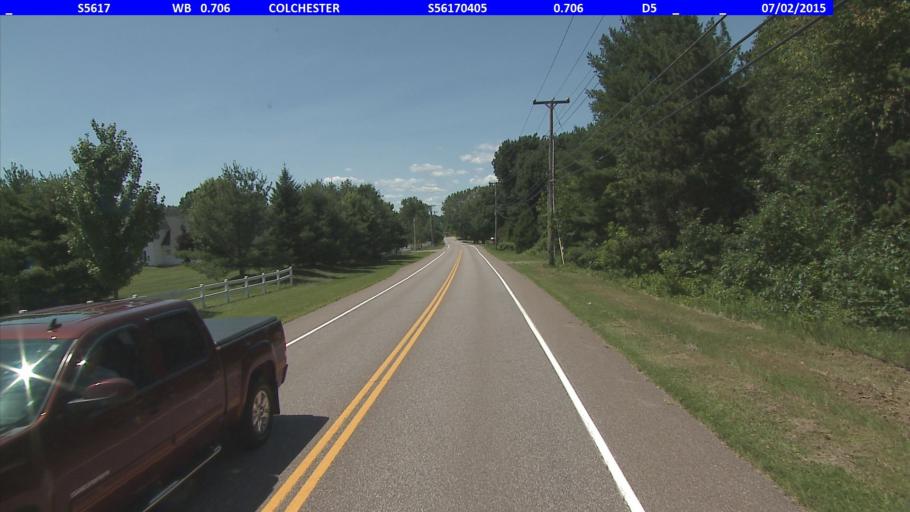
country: US
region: Vermont
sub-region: Chittenden County
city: Colchester
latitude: 44.5521
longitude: -73.1775
